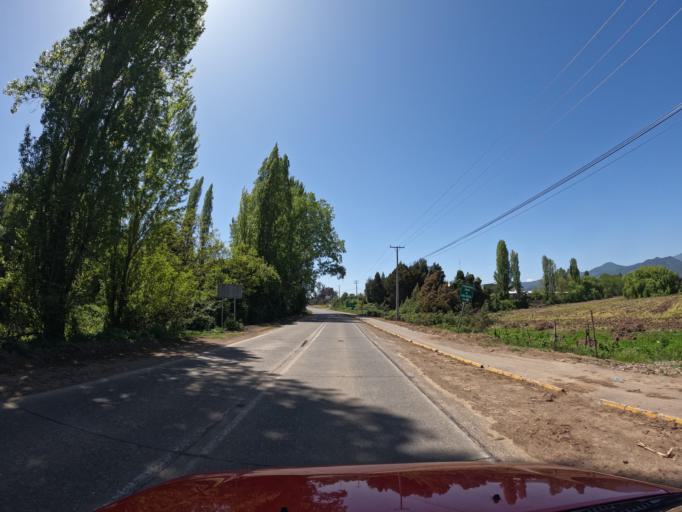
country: CL
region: Maule
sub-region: Provincia de Linares
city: Colbun
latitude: -35.7657
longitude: -71.4230
